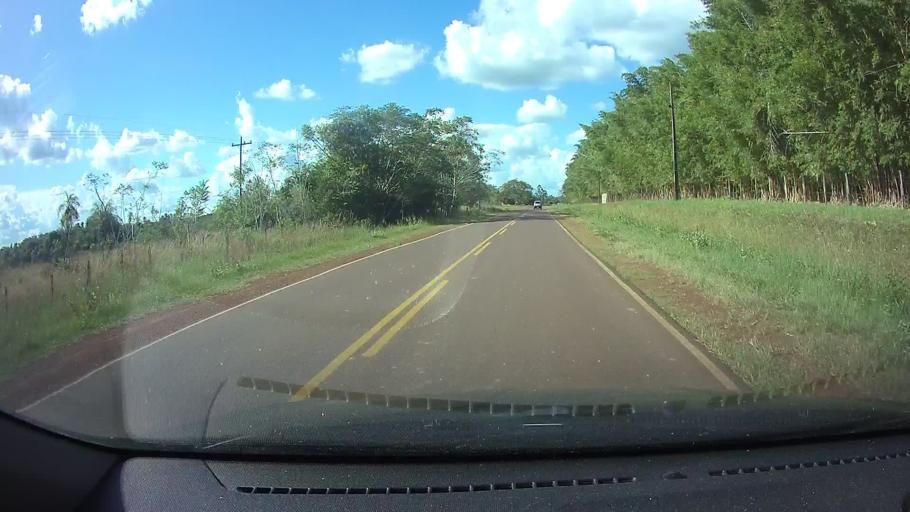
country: PY
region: Cordillera
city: Itacurubi de la Cordillera
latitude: -25.4740
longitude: -56.8812
